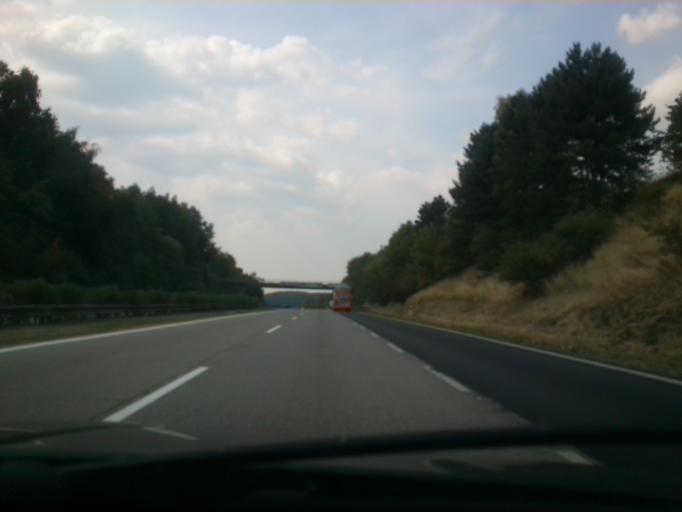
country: CZ
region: Central Bohemia
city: Divisov
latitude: 49.8250
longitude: 14.8684
